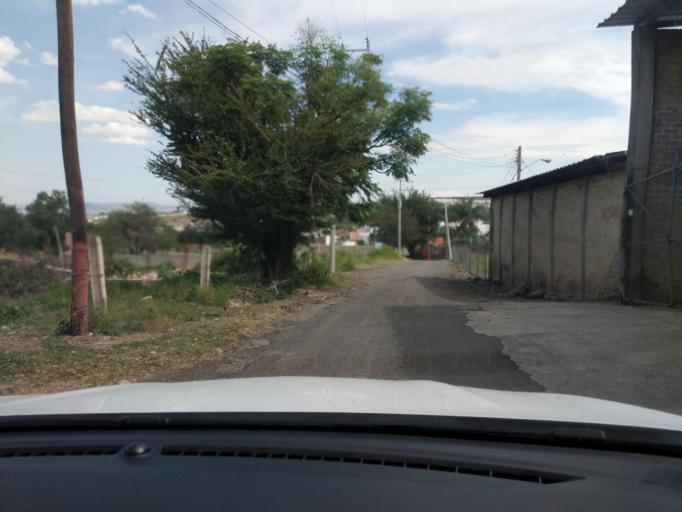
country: MX
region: Jalisco
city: Coyula
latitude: 20.6287
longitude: -103.2167
